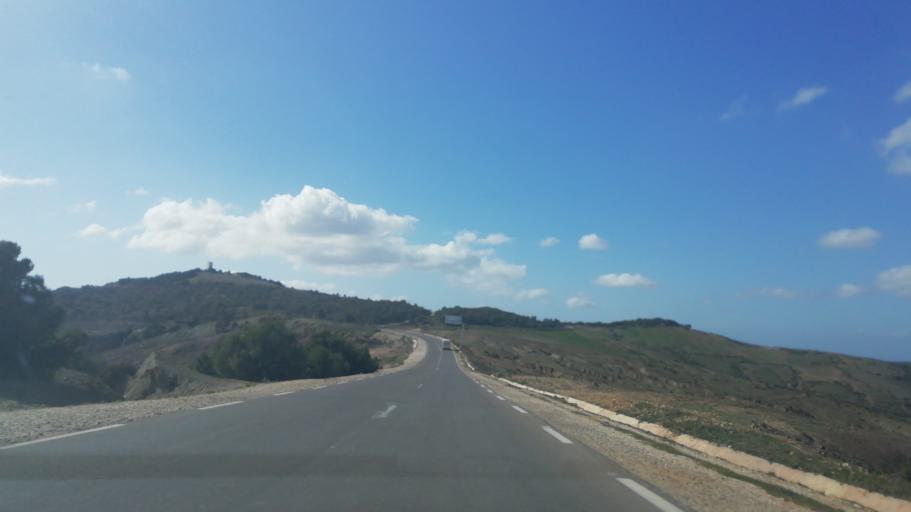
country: DZ
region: Relizane
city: Djidiouia
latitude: 36.0960
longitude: 0.5264
